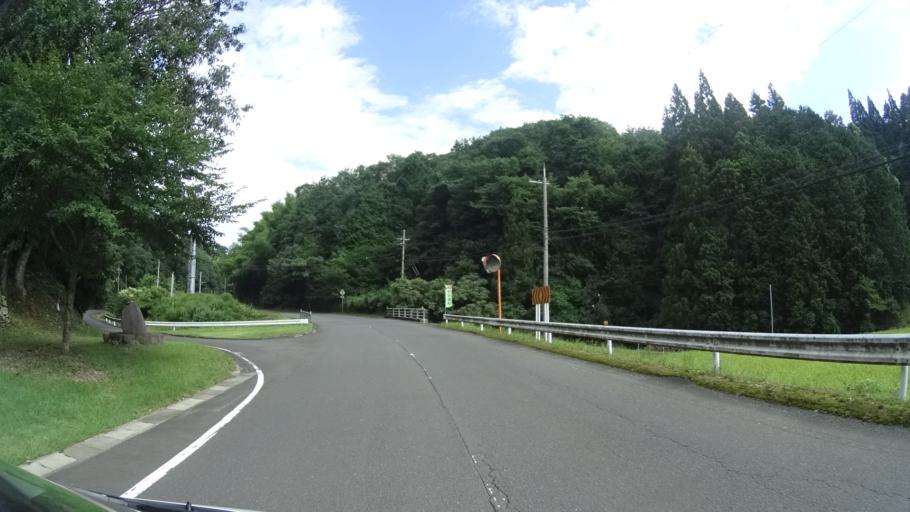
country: JP
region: Kyoto
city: Fukuchiyama
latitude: 35.3582
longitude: 135.1409
